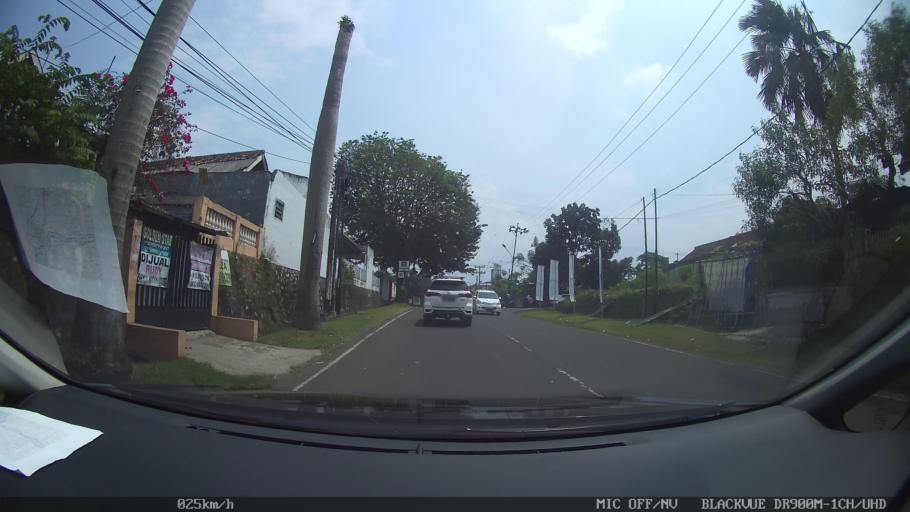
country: ID
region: Lampung
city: Bandarlampung
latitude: -5.4308
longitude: 105.2717
